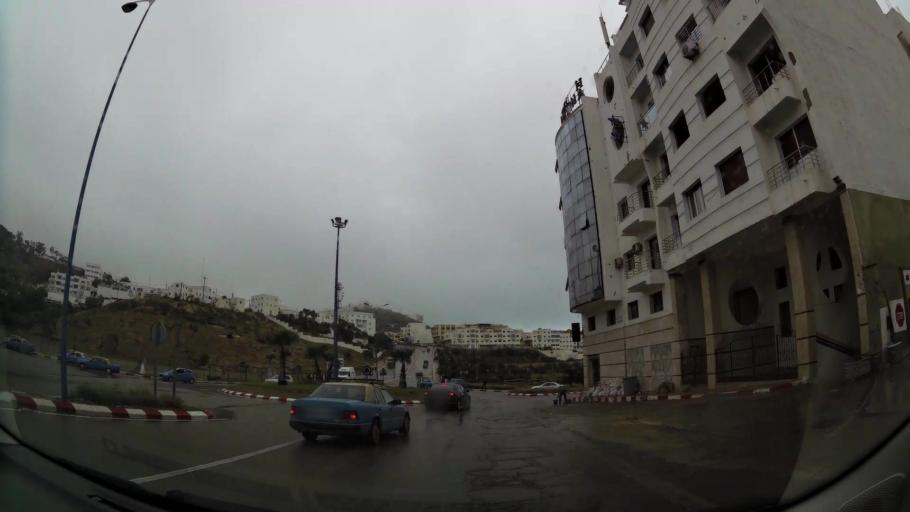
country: MA
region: Taza-Al Hoceima-Taounate
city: Al Hoceima
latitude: 35.2335
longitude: -3.9280
